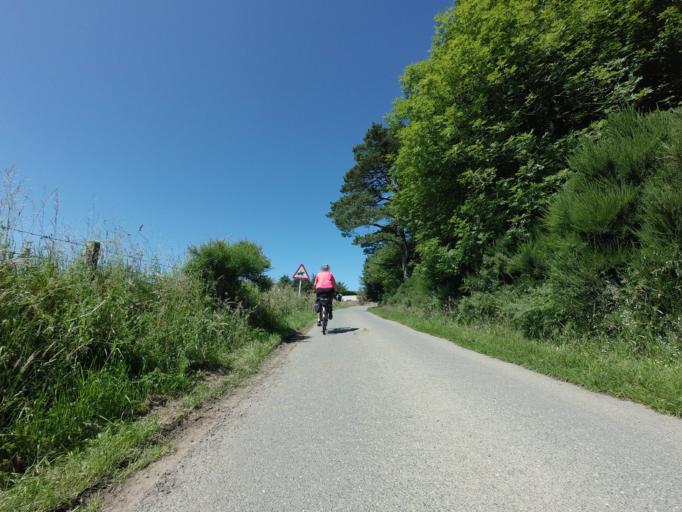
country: GB
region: Scotland
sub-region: Aberdeenshire
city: Macduff
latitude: 57.6436
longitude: -2.5075
